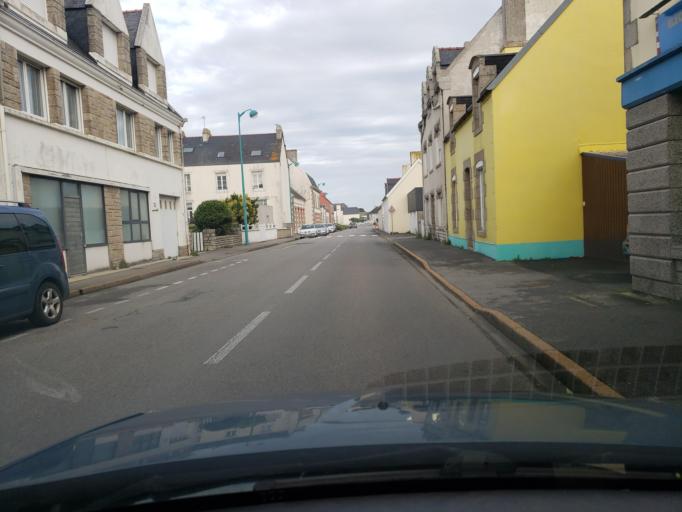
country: FR
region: Brittany
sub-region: Departement du Finistere
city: Guilvinec
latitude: 47.7962
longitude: -4.2728
